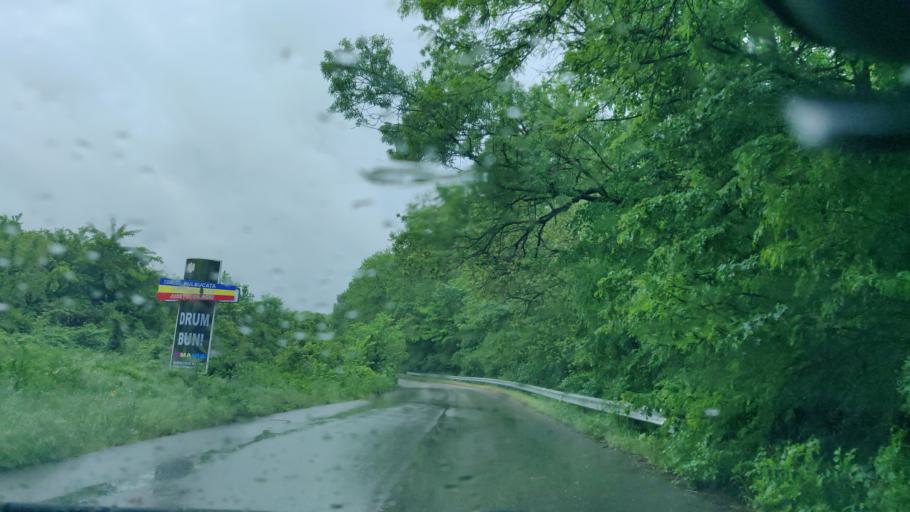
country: RO
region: Giurgiu
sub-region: Comuna Bulbucata
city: Bulbucata
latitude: 44.2890
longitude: 25.7785
